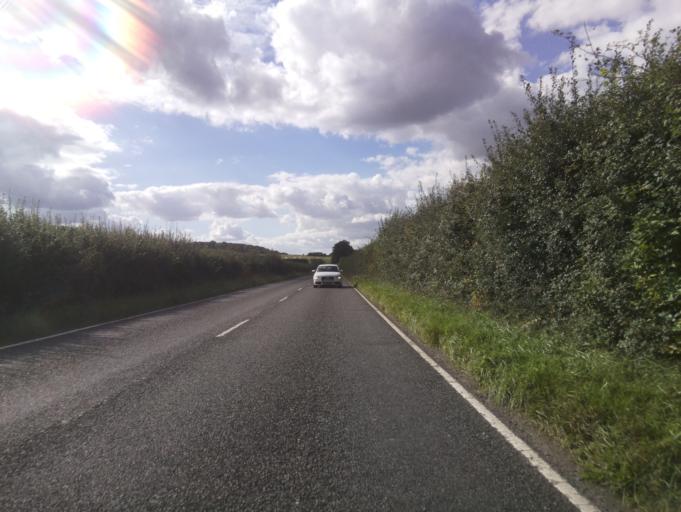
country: GB
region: England
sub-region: Hampshire
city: East Dean
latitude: 51.1131
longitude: -1.6039
